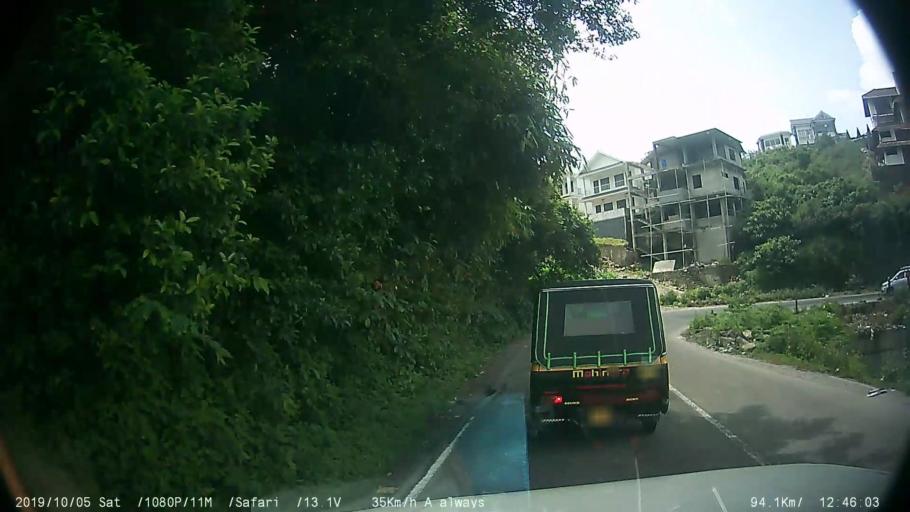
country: IN
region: Kerala
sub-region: Kottayam
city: Erattupetta
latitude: 9.5805
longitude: 76.9730
